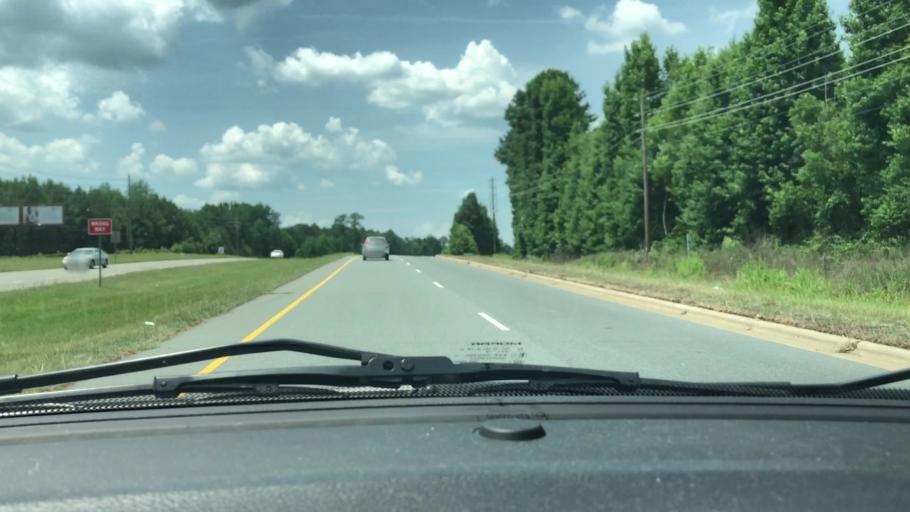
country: US
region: North Carolina
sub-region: Lee County
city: Sanford
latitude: 35.5006
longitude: -79.2030
